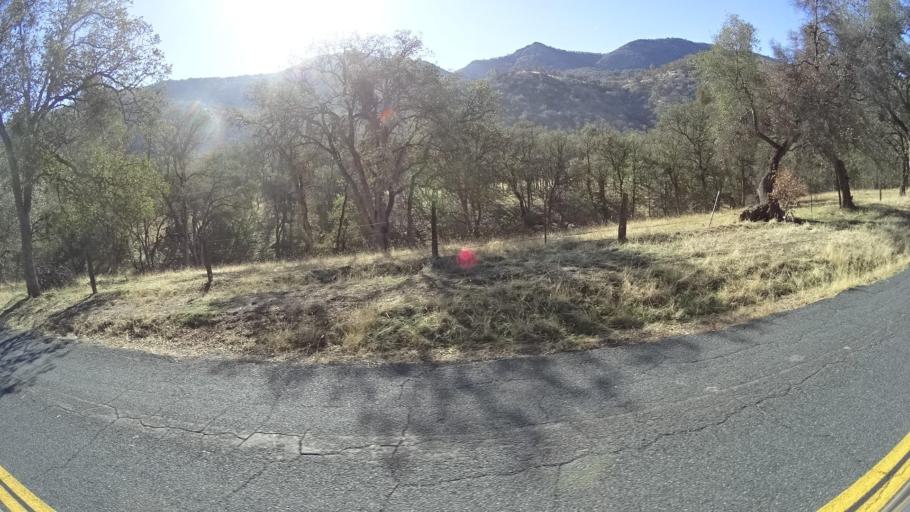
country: US
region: California
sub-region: Kern County
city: Alta Sierra
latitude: 35.7858
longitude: -118.7753
